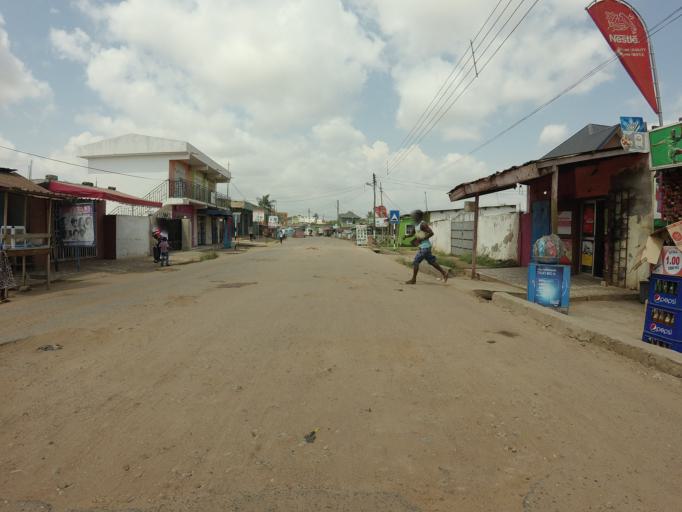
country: GH
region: Greater Accra
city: Dome
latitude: 5.6120
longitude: -0.2450
